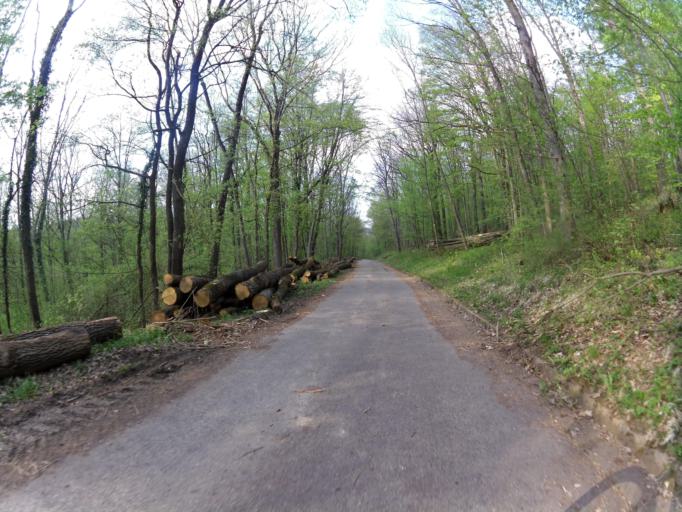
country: DE
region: Bavaria
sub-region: Regierungsbezirk Unterfranken
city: Winterhausen
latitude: 49.6970
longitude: 10.0034
